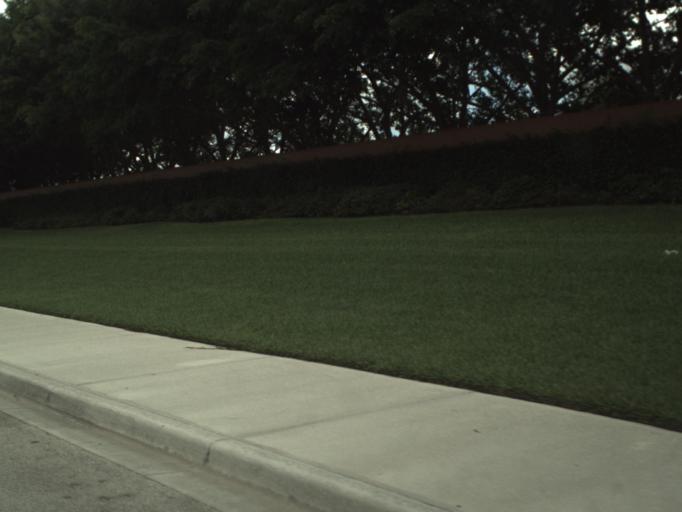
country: US
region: Florida
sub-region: Palm Beach County
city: Wellington
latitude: 26.6509
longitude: -80.1921
